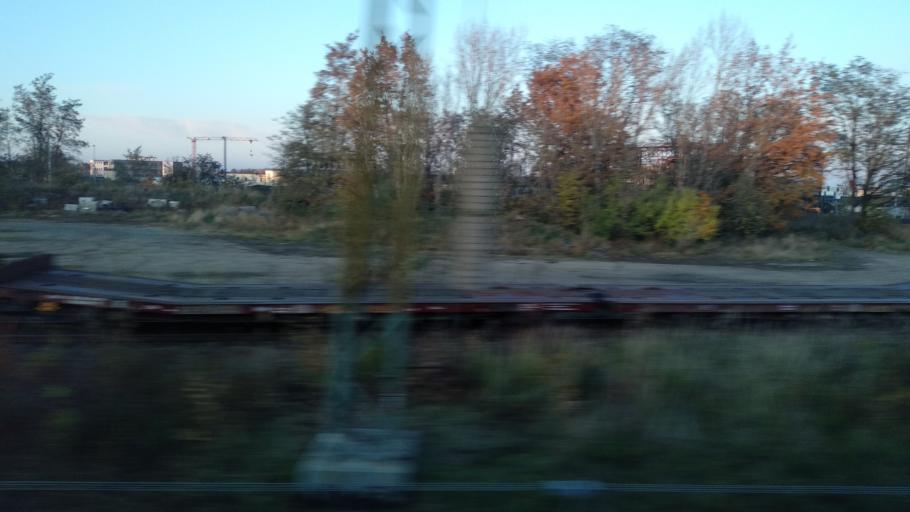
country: DE
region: Saxony
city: Riesa
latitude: 51.3119
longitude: 13.2689
